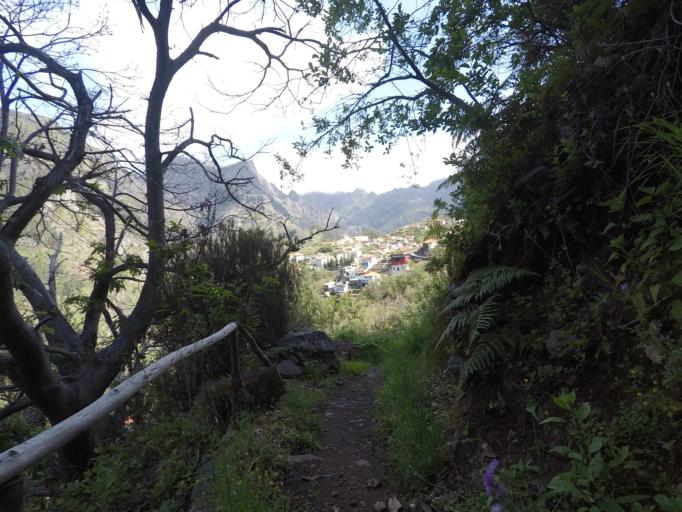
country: PT
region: Madeira
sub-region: Camara de Lobos
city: Curral das Freiras
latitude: 32.7161
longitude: -16.9642
